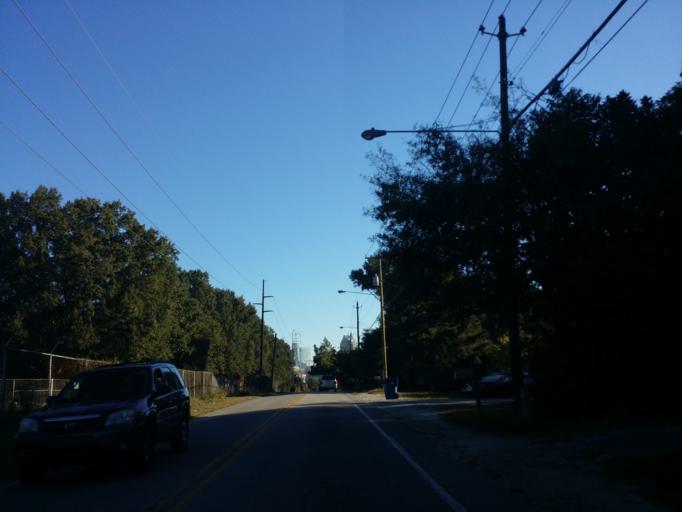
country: US
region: North Carolina
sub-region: Wake County
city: Raleigh
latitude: 35.7655
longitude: -78.6544
